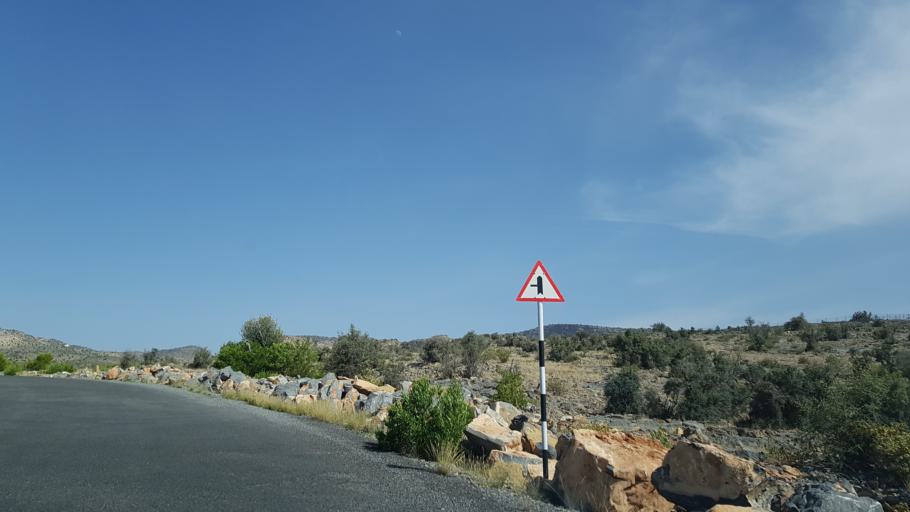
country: OM
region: Al Batinah
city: Bayt al `Awabi
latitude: 23.1418
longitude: 57.5358
